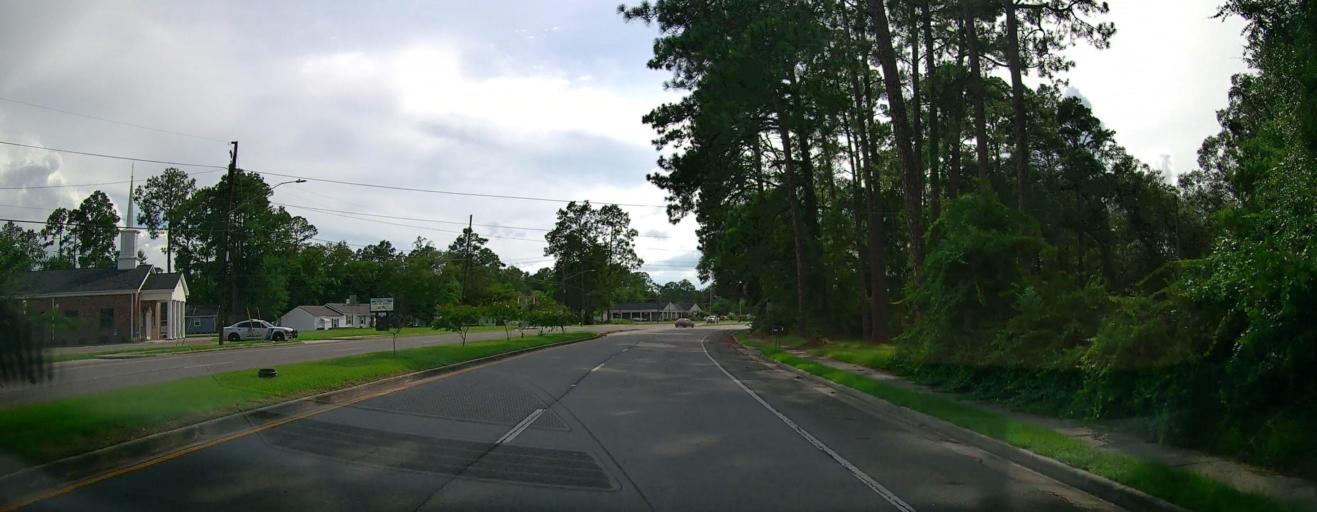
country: US
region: Georgia
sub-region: Wayne County
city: Jesup
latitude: 31.6022
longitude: -81.8916
